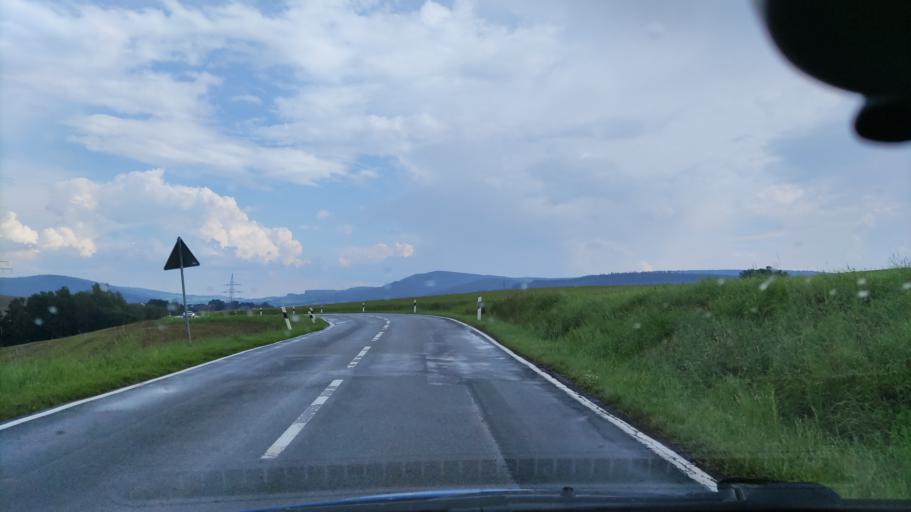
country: DE
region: Lower Saxony
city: Delligsen
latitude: 51.9550
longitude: 9.7884
